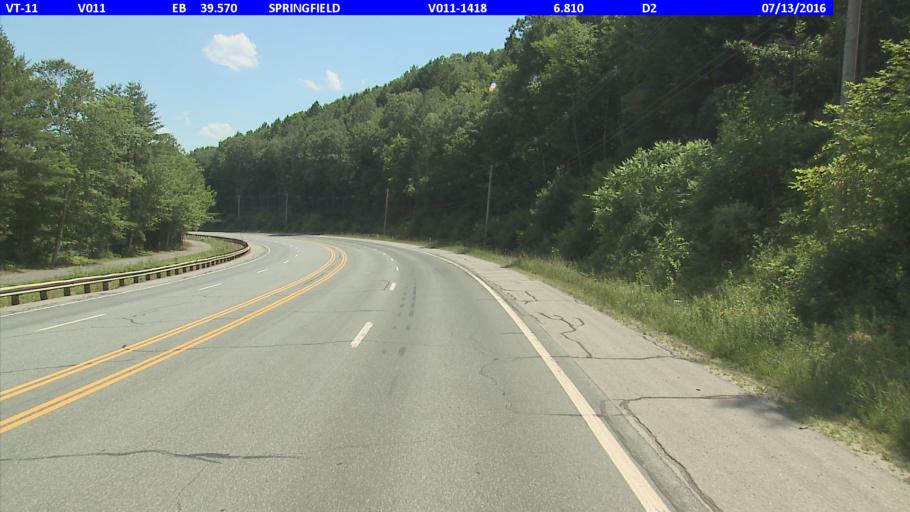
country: US
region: Vermont
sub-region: Windsor County
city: Springfield
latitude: 43.2729
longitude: -72.4607
